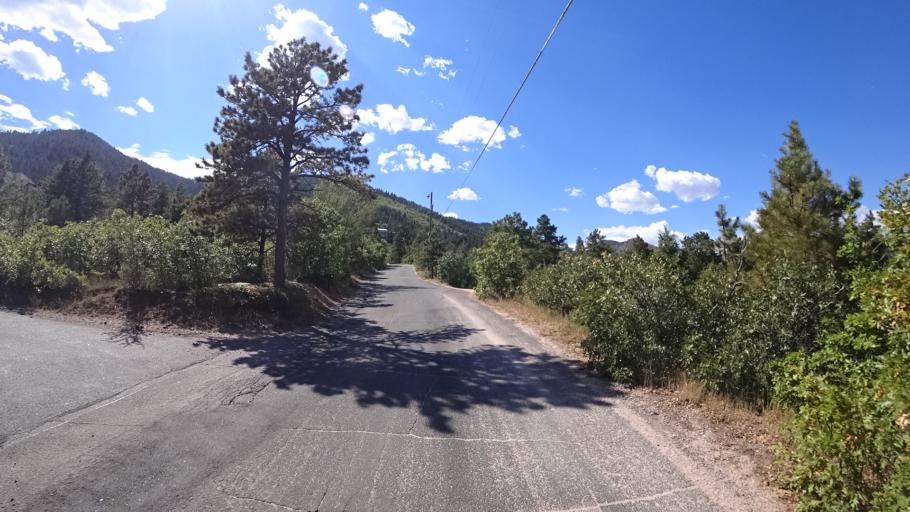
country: US
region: Colorado
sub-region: El Paso County
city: Colorado Springs
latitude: 38.8128
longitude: -104.8777
